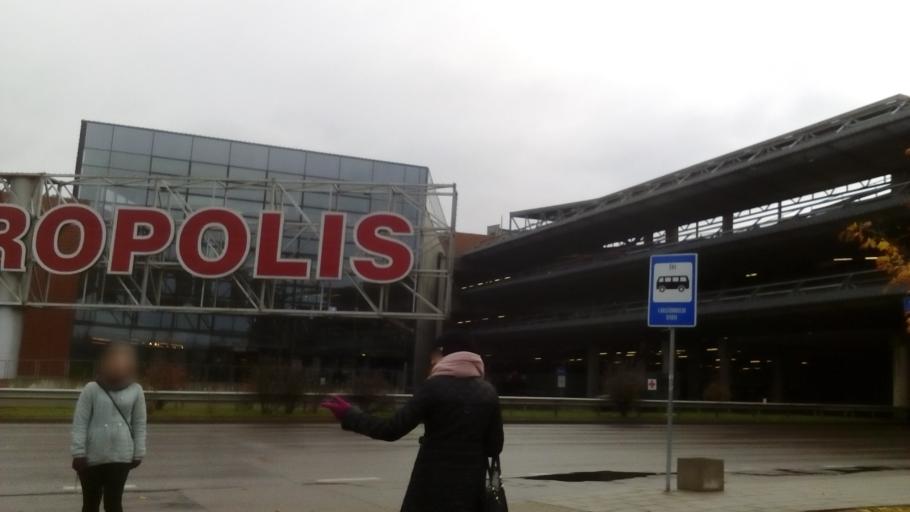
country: LT
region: Kauno apskritis
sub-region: Kaunas
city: Kaunas
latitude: 54.8920
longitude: 23.9164
